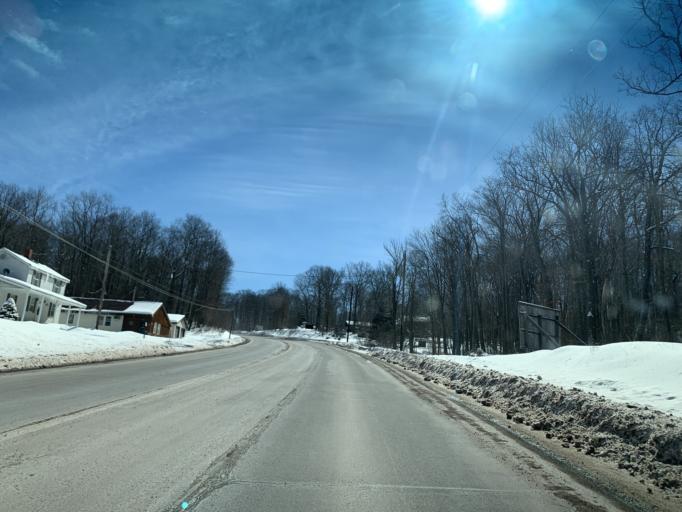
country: US
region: Pennsylvania
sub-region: Somerset County
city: Meyersdale
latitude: 39.7251
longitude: -79.3136
